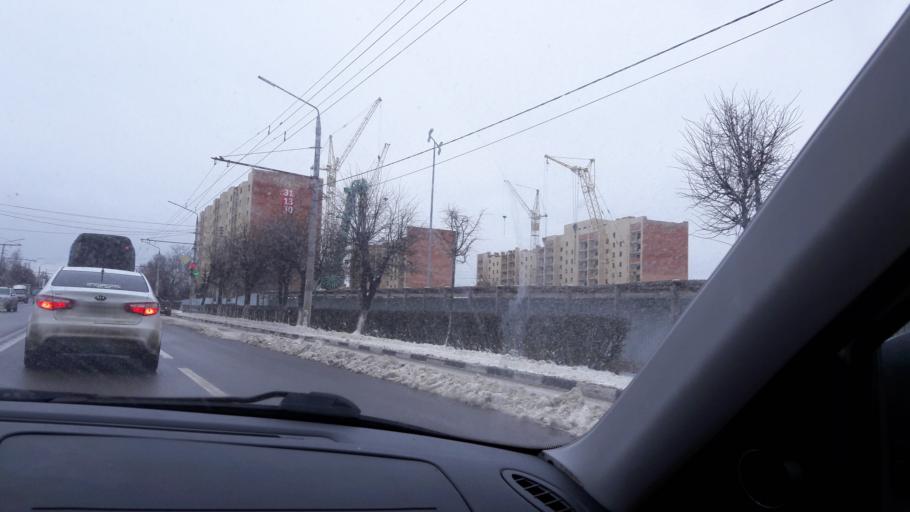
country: RU
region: Tula
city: Gorelki
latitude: 54.2326
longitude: 37.6249
